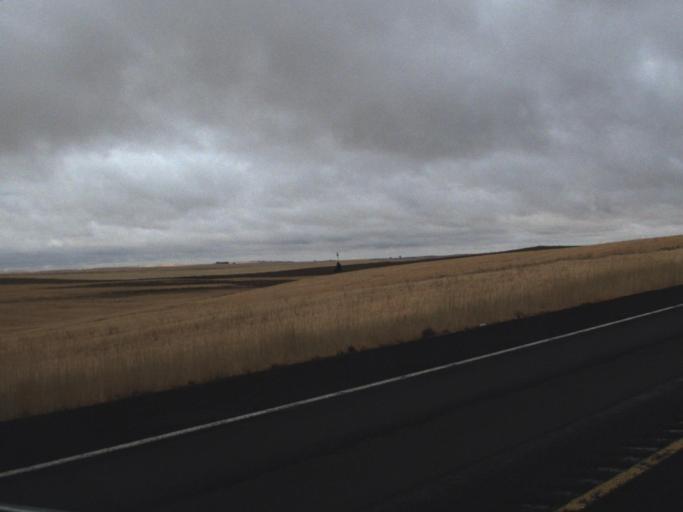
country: US
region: Washington
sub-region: Lincoln County
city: Davenport
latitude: 47.6478
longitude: -118.1914
